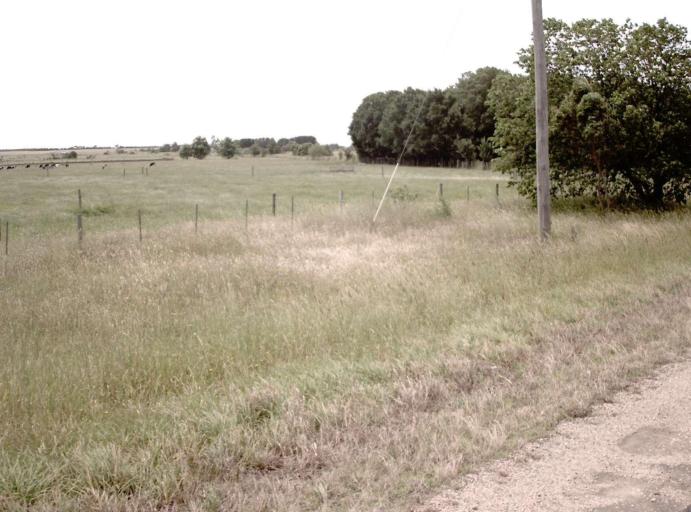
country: AU
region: Victoria
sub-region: Wellington
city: Sale
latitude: -37.9955
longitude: 147.0000
